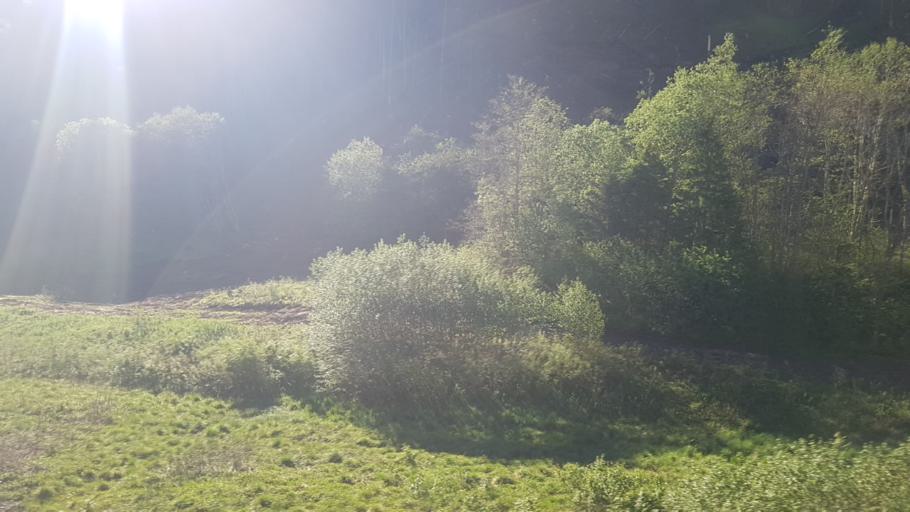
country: NO
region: Sor-Trondelag
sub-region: Melhus
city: Melhus
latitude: 63.2494
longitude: 10.2734
